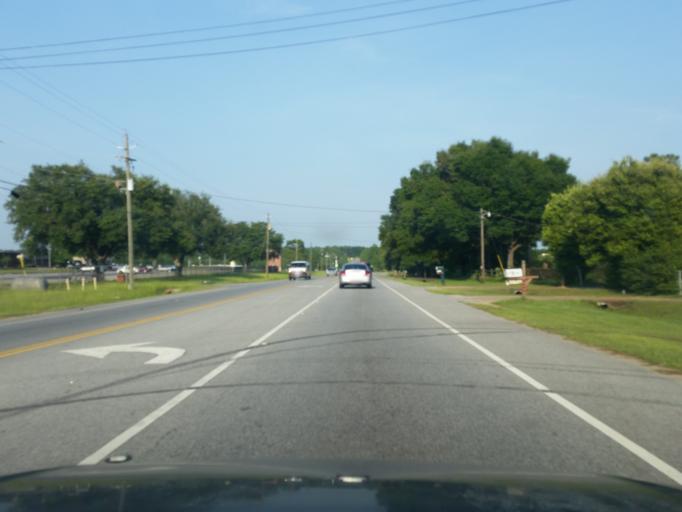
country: US
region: Florida
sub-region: Escambia County
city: Bellview
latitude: 30.4864
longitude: -87.2940
